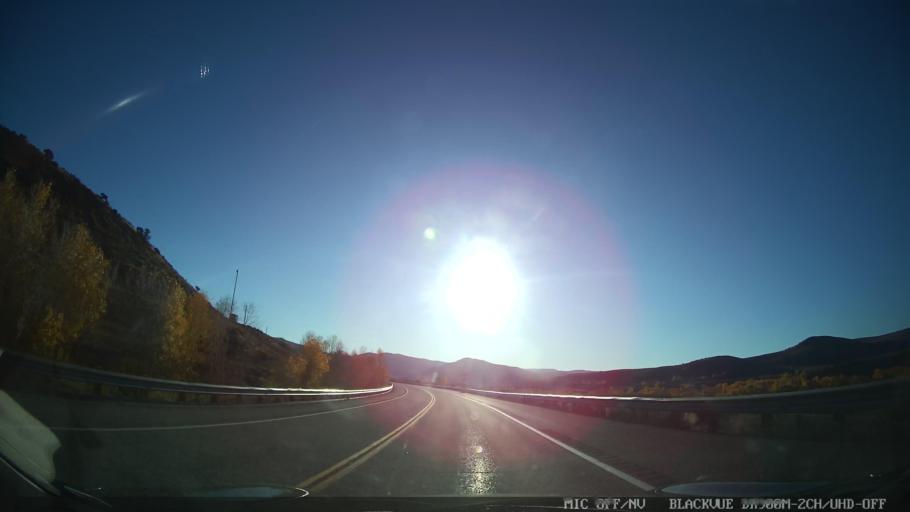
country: US
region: Colorado
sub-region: Grand County
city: Hot Sulphur Springs
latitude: 40.0521
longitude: -106.1709
